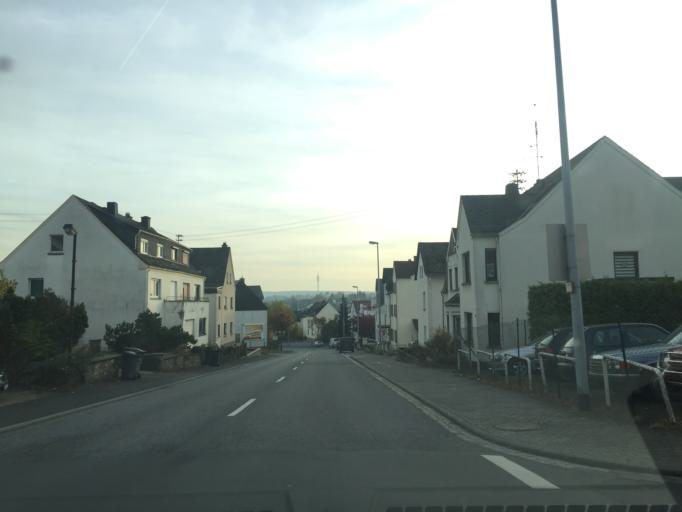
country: DE
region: Hesse
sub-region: Regierungsbezirk Giessen
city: Elz
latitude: 50.4156
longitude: 8.0296
